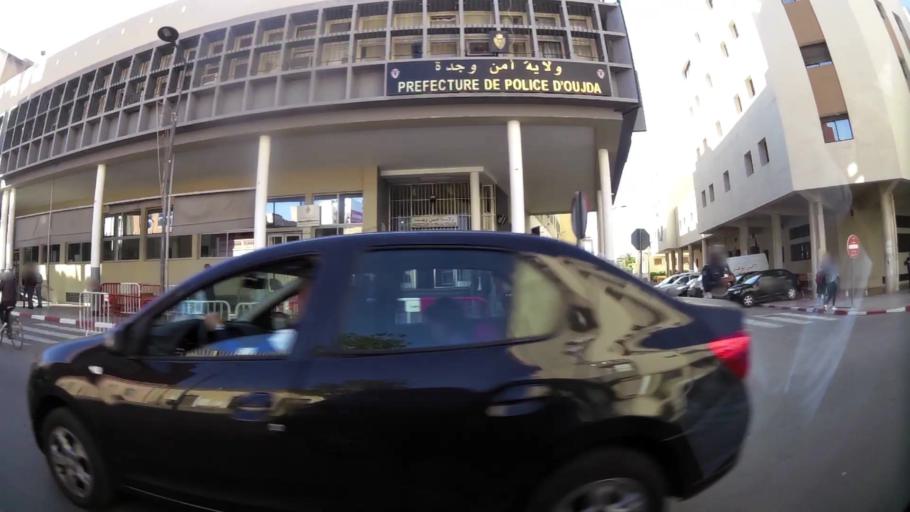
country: MA
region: Oriental
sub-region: Oujda-Angad
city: Oujda
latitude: 34.6820
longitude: -1.9190
